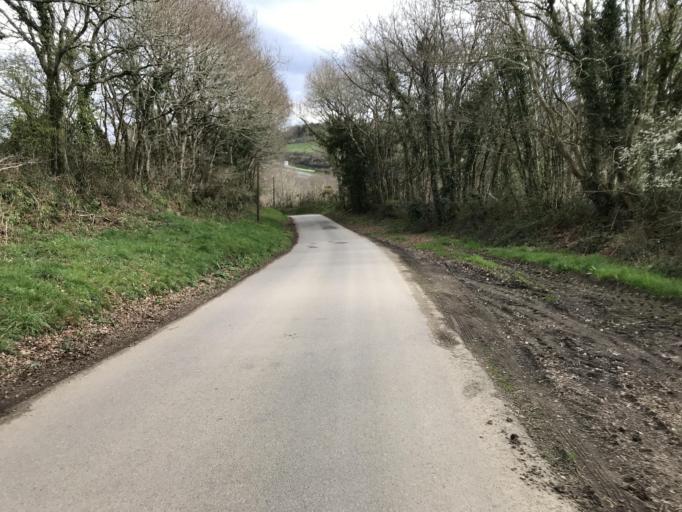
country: FR
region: Brittany
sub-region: Departement du Finistere
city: Hopital-Camfrout
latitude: 48.3161
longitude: -4.2111
